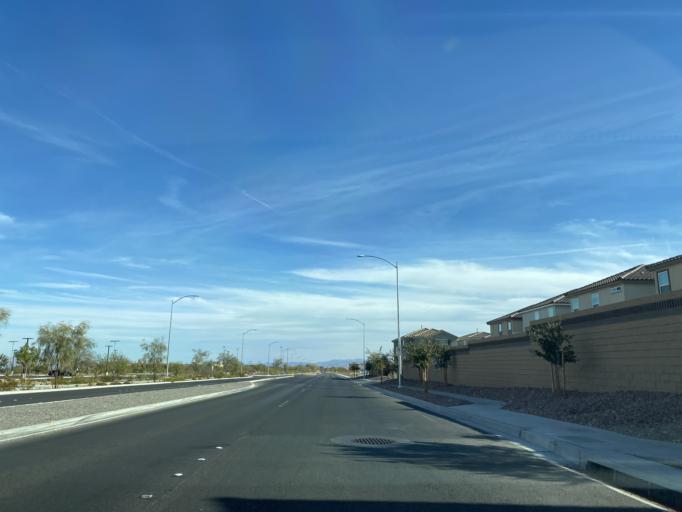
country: US
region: Nevada
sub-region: Clark County
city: Enterprise
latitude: 36.0482
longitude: -115.2760
